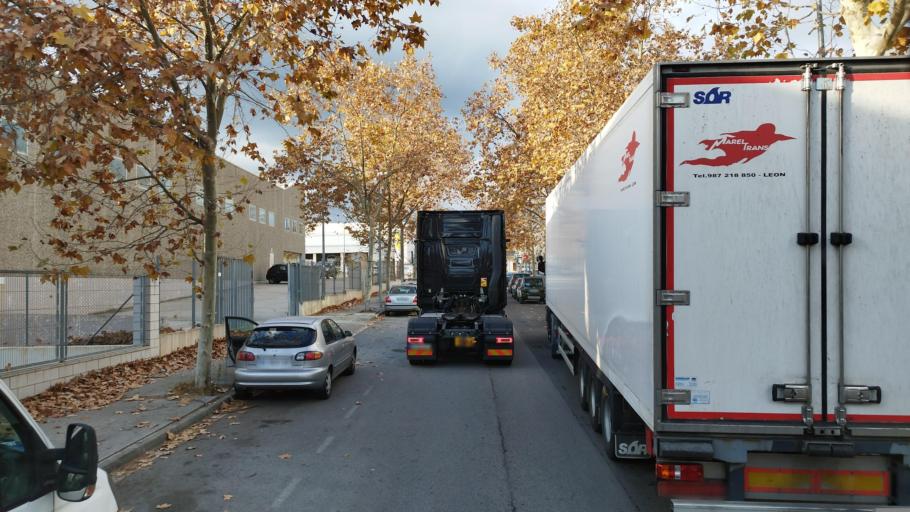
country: ES
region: Catalonia
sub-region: Provincia de Barcelona
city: Vilanova i la Geltru
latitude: 41.2325
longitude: 1.7404
